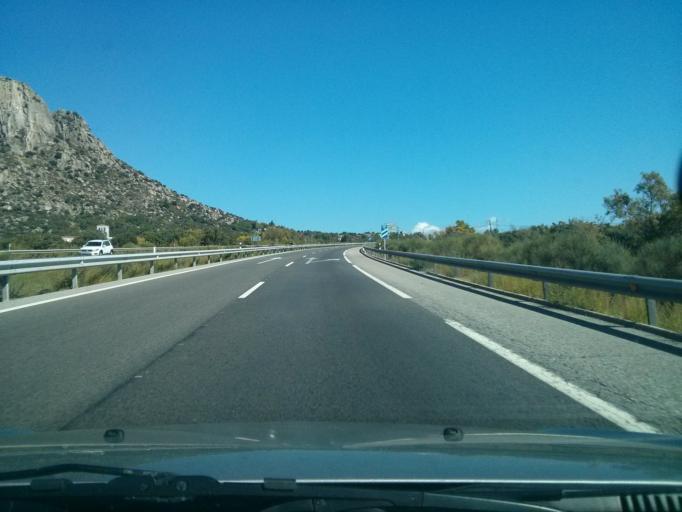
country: ES
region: Madrid
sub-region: Provincia de Madrid
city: La Cabrera
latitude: 40.8670
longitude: -3.6054
